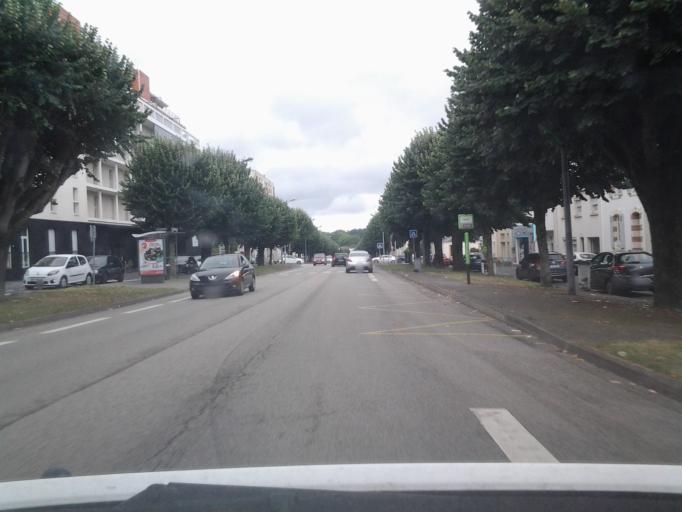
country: FR
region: Pays de la Loire
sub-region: Departement de la Vendee
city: La Roche-sur-Yon
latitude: 46.6749
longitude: -1.4236
